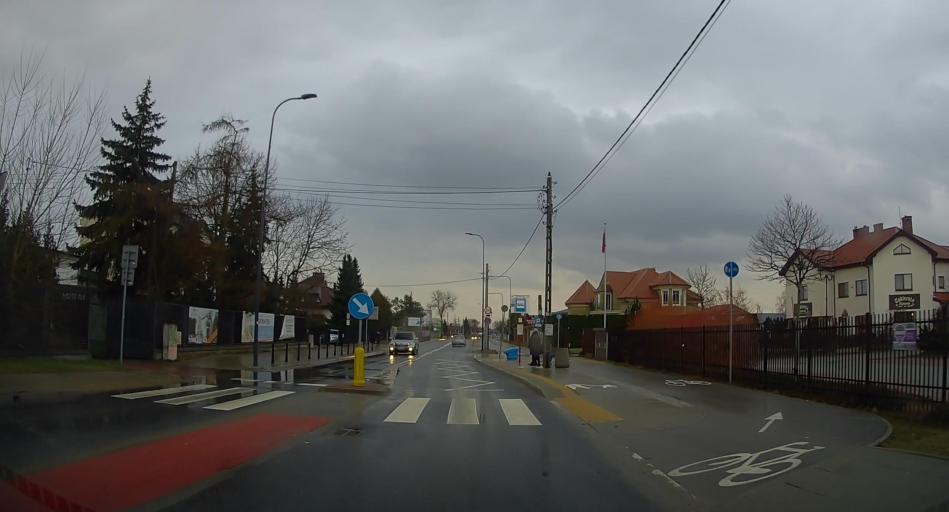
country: PL
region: Masovian Voivodeship
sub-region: Warszawa
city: Wawer
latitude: 52.1965
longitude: 21.1360
